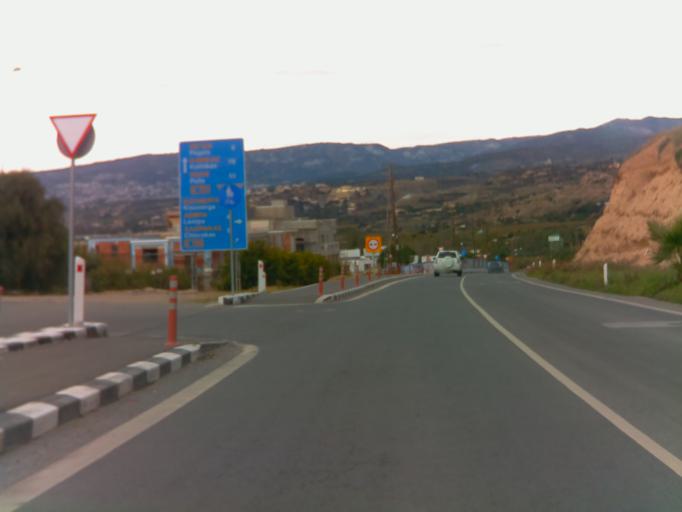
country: CY
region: Pafos
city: Kissonerga
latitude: 34.8290
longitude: 32.3923
